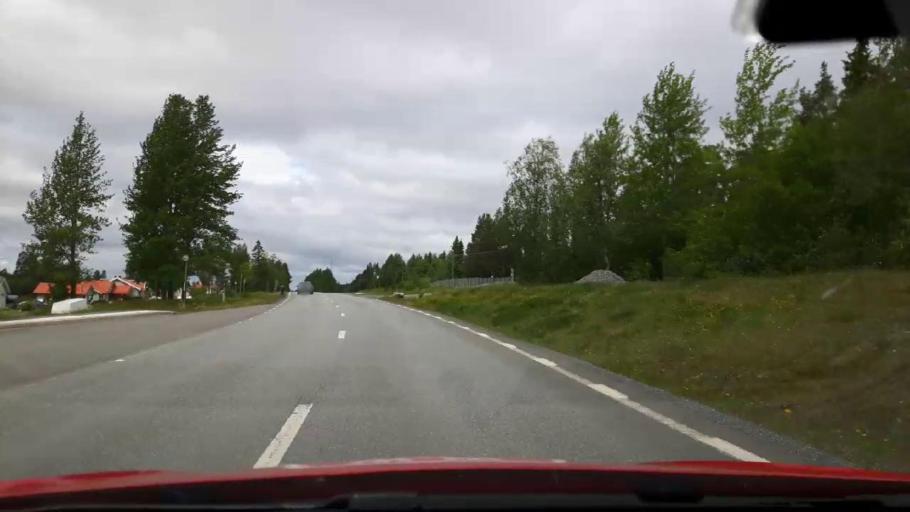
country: SE
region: Jaemtland
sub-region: Krokoms Kommun
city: Krokom
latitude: 63.2908
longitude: 14.4942
